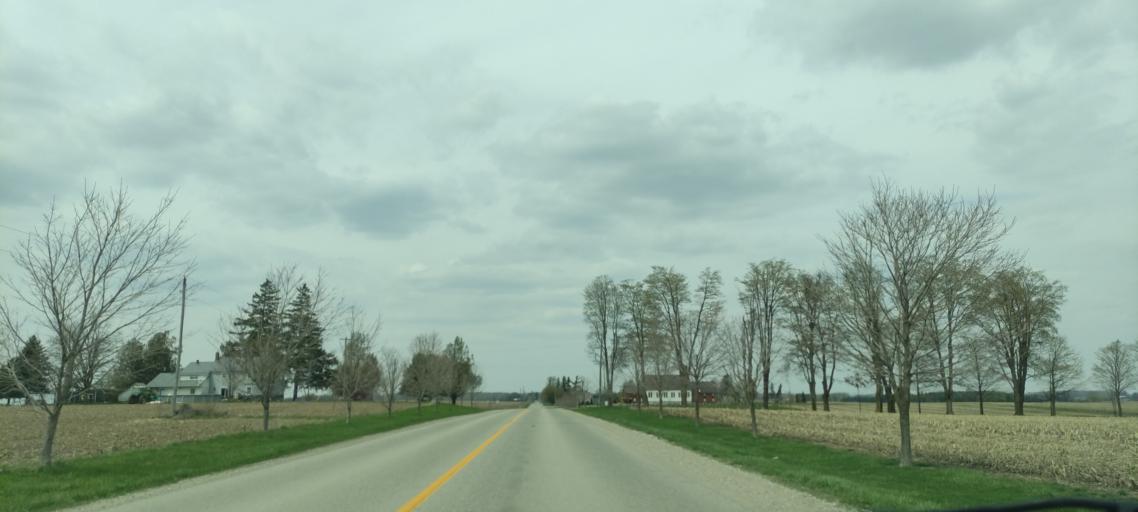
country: CA
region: Ontario
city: Stratford
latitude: 43.3191
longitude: -80.7846
